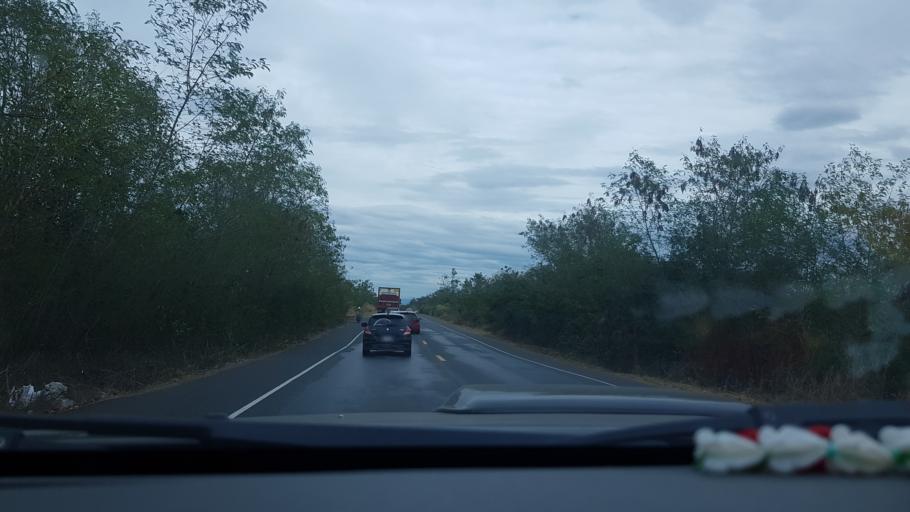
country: TH
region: Phetchabun
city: Phetchabun
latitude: 16.4763
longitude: 101.1315
